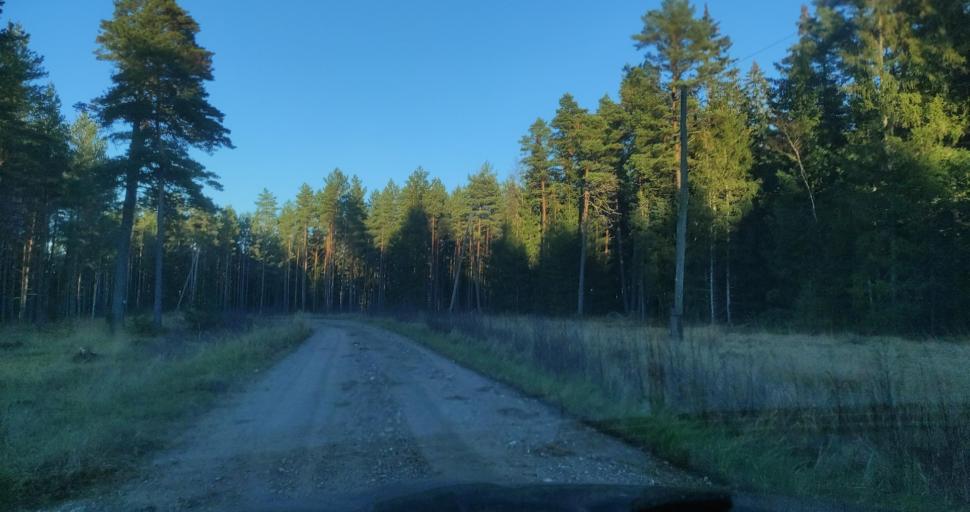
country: LV
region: Dundaga
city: Dundaga
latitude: 57.3780
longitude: 22.0815
